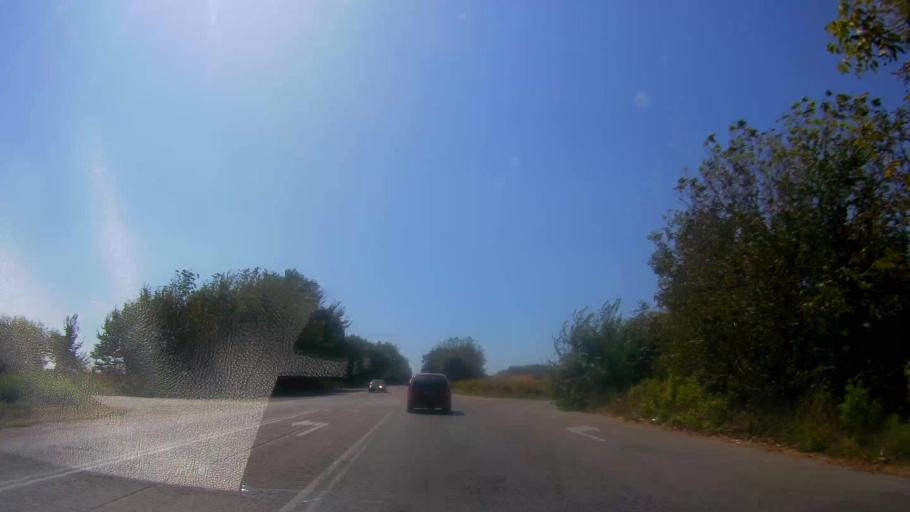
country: BG
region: Veliko Turnovo
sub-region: Obshtina Gorna Oryakhovitsa
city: Purvomaytsi
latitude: 43.2410
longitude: 25.6424
